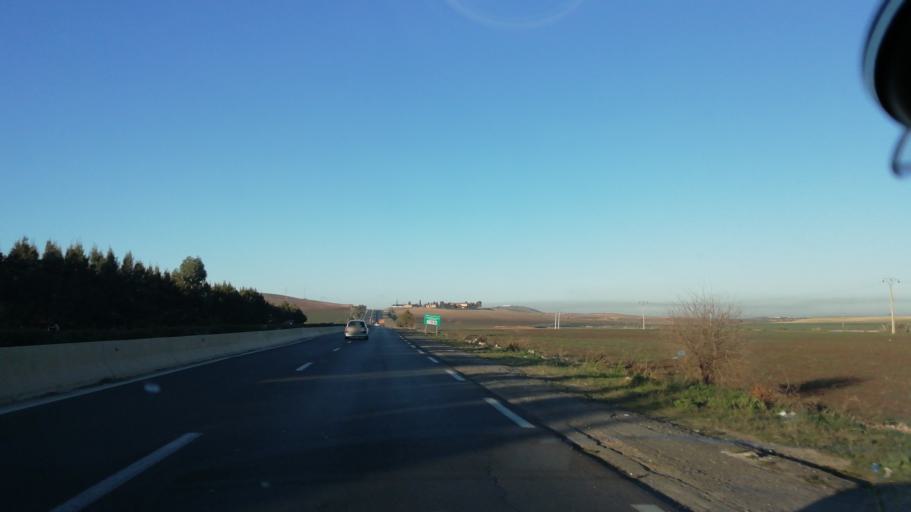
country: DZ
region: Ain Temouchent
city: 'Ain Temouchent
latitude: 35.2944
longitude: -1.1912
